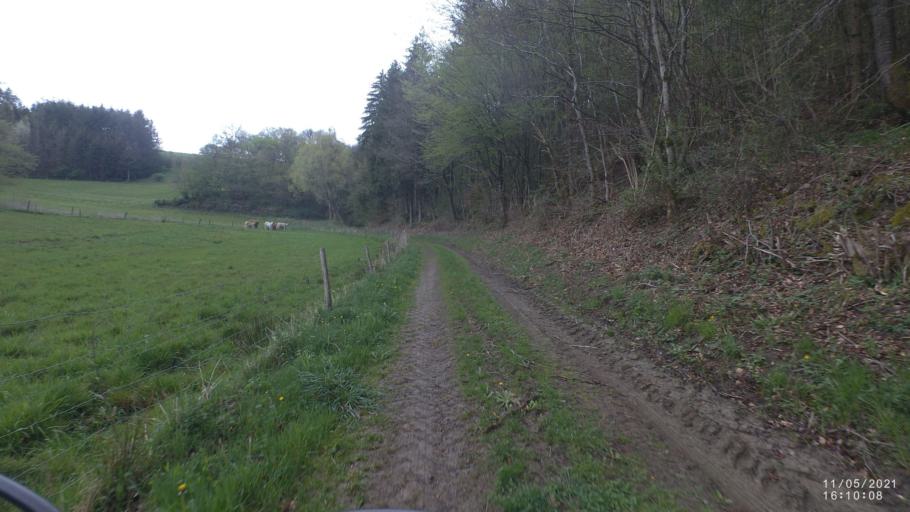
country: DE
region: Rheinland-Pfalz
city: Nachtsheim
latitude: 50.3115
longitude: 7.0680
